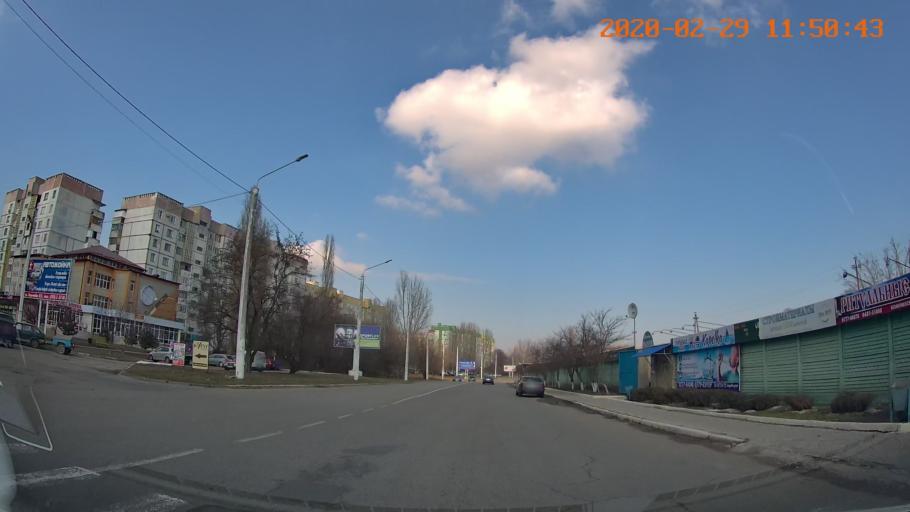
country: MD
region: Telenesti
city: Ribnita
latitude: 47.7602
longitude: 28.9900
